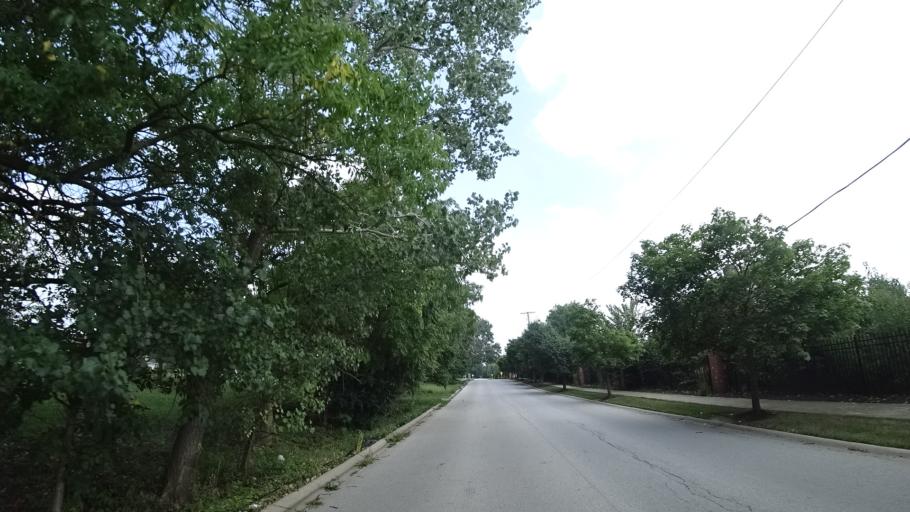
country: US
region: Illinois
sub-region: Cook County
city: Orland Park
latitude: 41.6371
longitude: -87.8908
